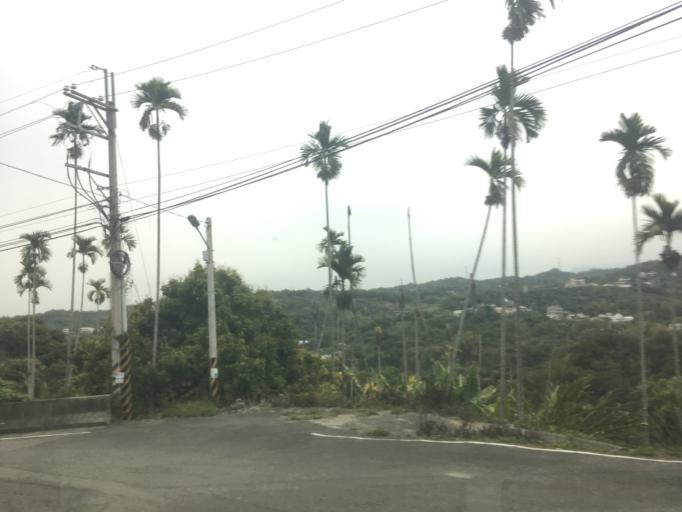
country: TW
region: Taiwan
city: Zhongxing New Village
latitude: 24.0313
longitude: 120.7234
